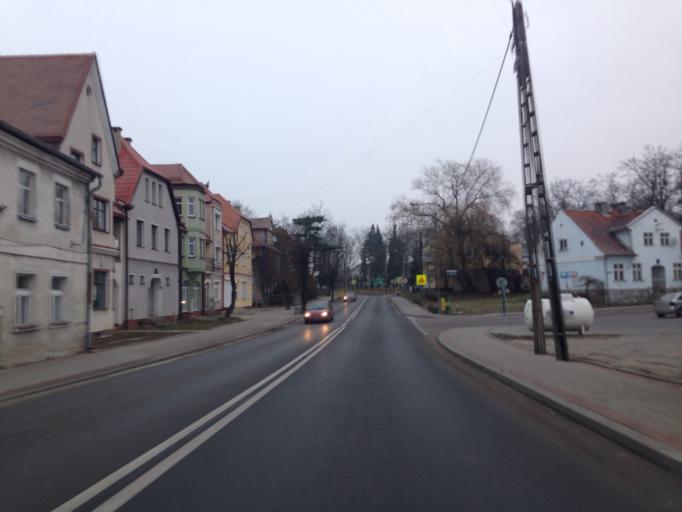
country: PL
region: Warmian-Masurian Voivodeship
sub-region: Powiat olsztynski
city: Biskupiec
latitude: 53.8638
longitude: 20.9573
